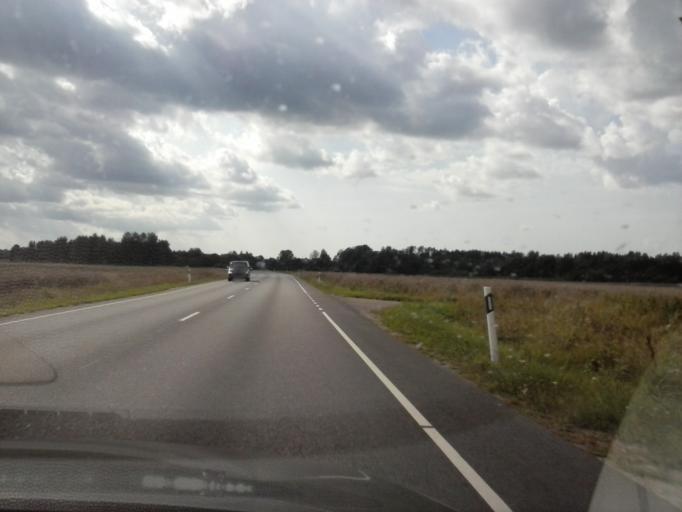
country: EE
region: Jaervamaa
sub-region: Tueri vald
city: Sarevere
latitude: 58.7548
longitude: 25.3402
